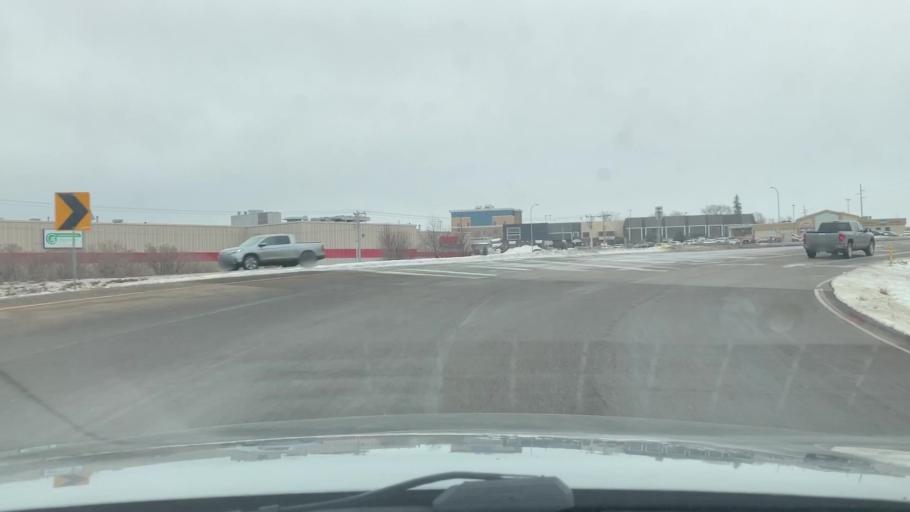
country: US
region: North Dakota
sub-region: Burleigh County
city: Bismarck
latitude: 46.8276
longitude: -100.8136
